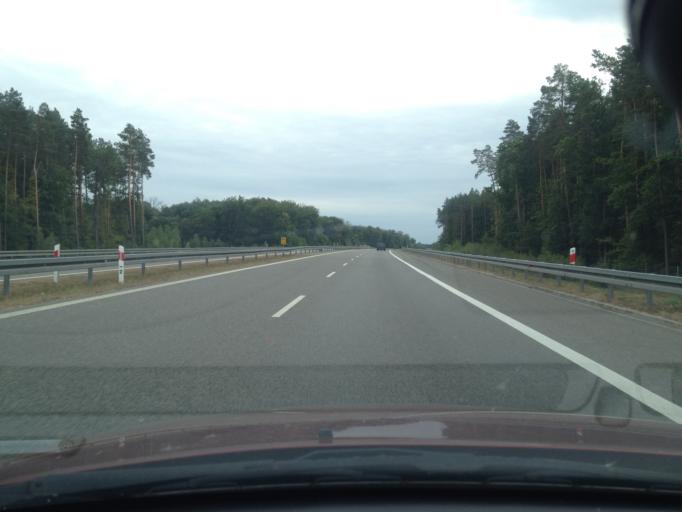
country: PL
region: West Pomeranian Voivodeship
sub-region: Powiat mysliborski
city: Nowogrodek Pomorski
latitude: 52.8605
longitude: 15.0354
